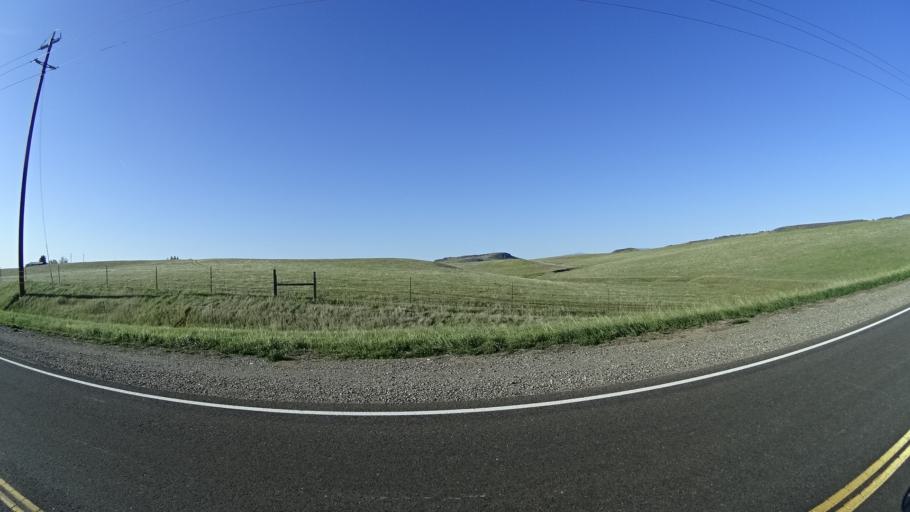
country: US
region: California
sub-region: Glenn County
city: Orland
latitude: 39.7881
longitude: -122.3065
